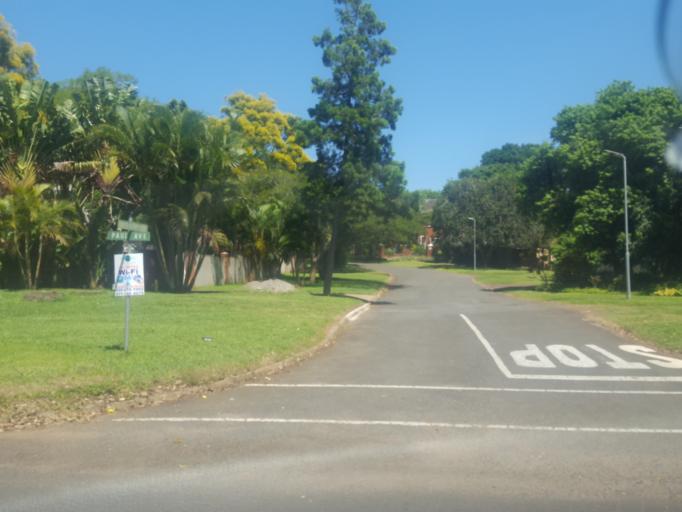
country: ZA
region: KwaZulu-Natal
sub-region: uThungulu District Municipality
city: Empangeni
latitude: -28.7437
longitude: 31.9021
